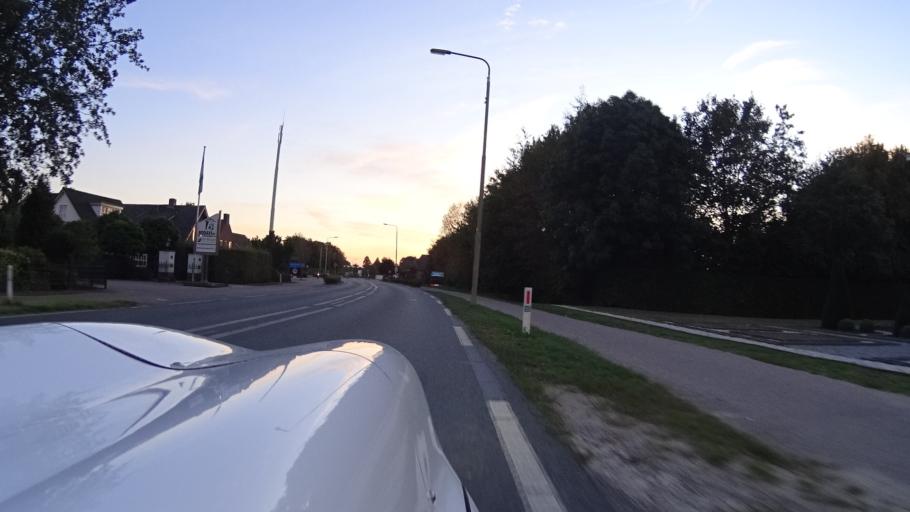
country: NL
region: Gelderland
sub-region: Gemeente Maasdriel
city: Hedel
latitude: 51.7484
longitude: 5.2373
